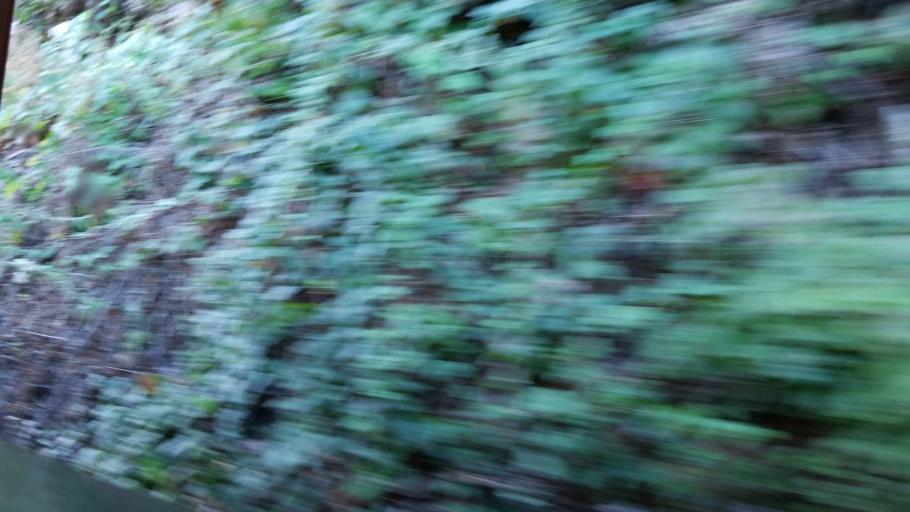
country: US
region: California
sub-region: Mendocino County
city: Fort Bragg
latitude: 39.4480
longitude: -123.7954
